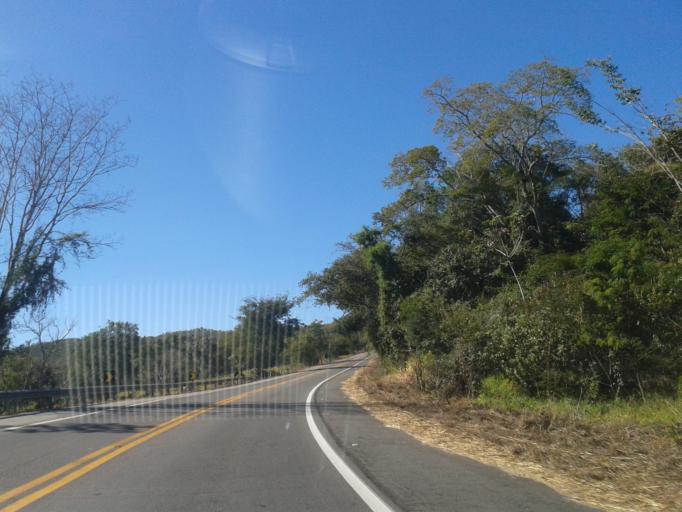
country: BR
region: Goias
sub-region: Goias
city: Goias
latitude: -15.8848
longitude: -50.1061
